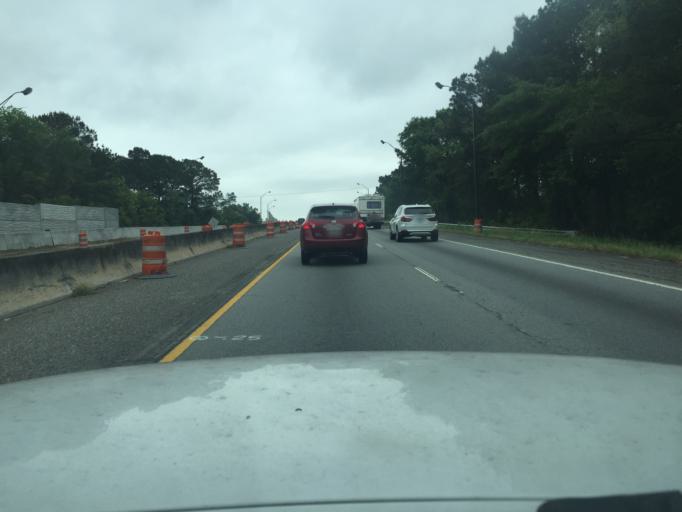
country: US
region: Georgia
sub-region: Chatham County
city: Georgetown
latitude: 31.9893
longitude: -81.2242
